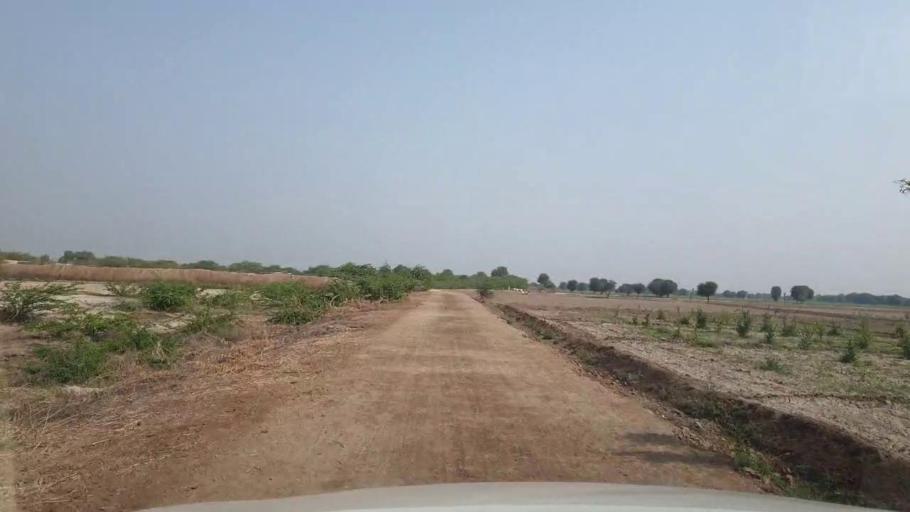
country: PK
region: Sindh
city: Chor
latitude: 25.4692
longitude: 69.7081
